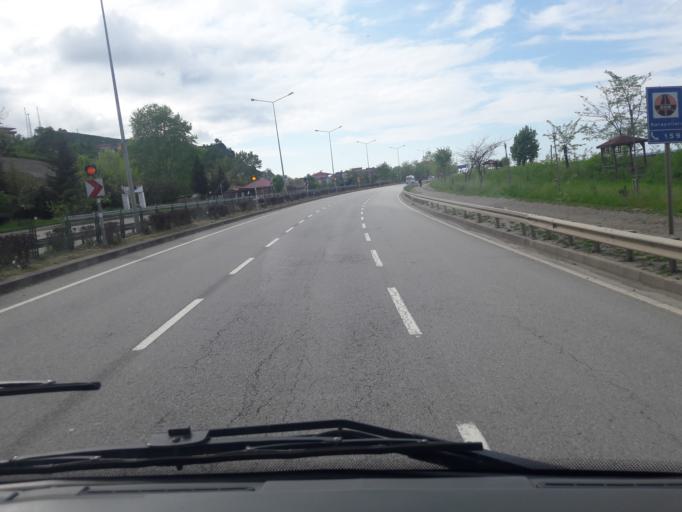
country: TR
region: Giresun
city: Piraziz
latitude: 40.9541
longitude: 38.1223
